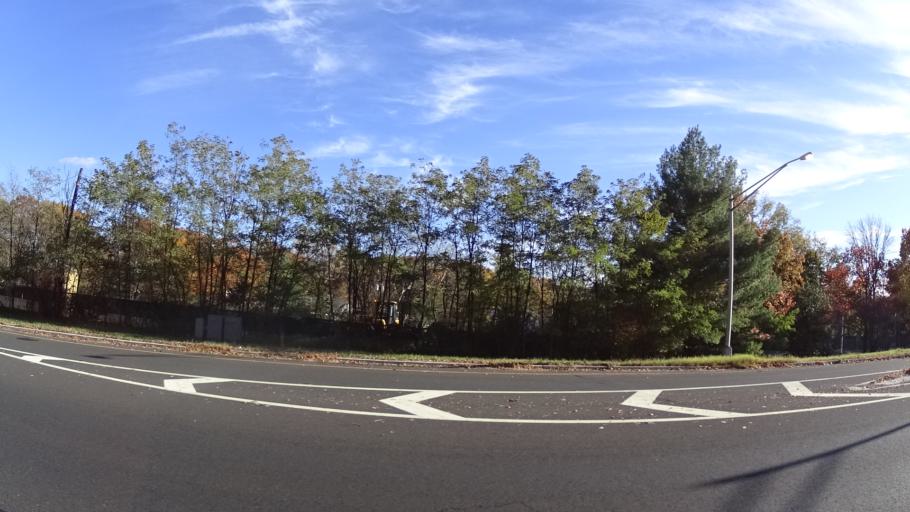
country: US
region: New Jersey
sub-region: Union County
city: Mountainside
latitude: 40.6743
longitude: -74.3512
